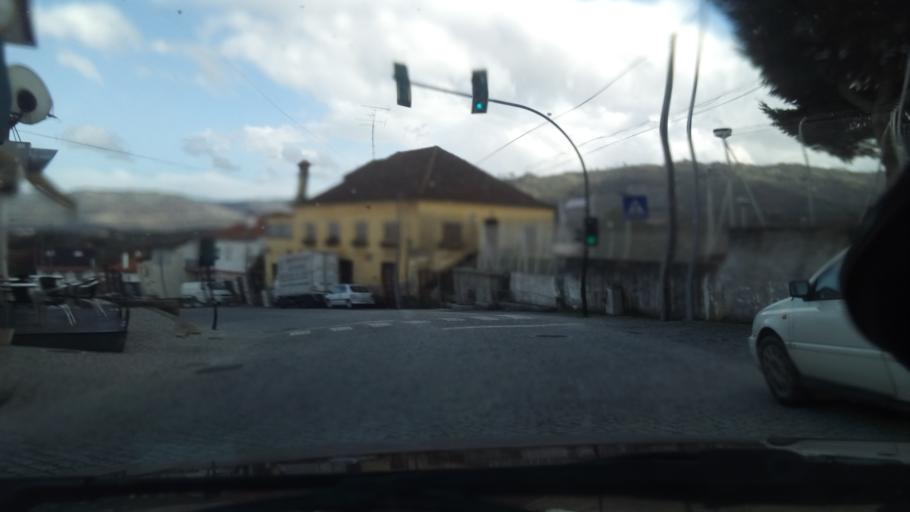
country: PT
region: Guarda
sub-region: Celorico da Beira
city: Celorico da Beira
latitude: 40.6273
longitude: -7.3405
